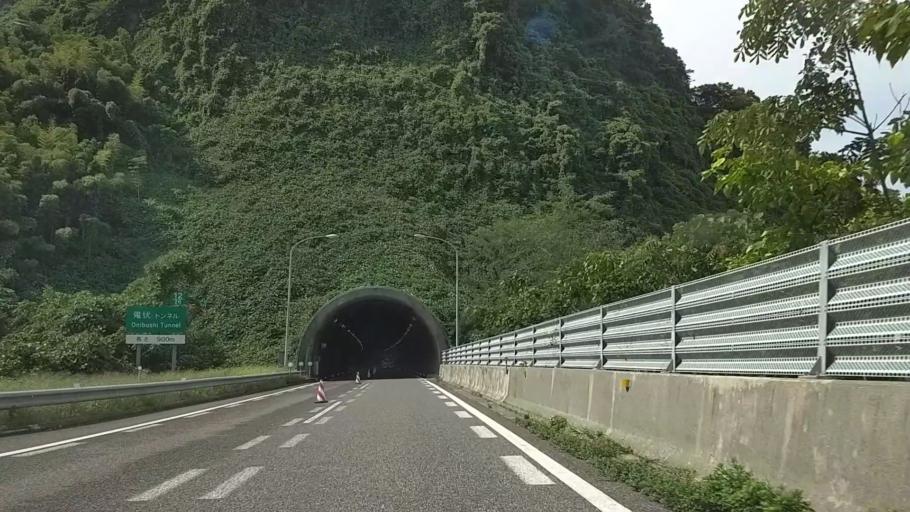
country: JP
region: Niigata
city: Itoigawa
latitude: 37.0826
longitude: 137.9497
